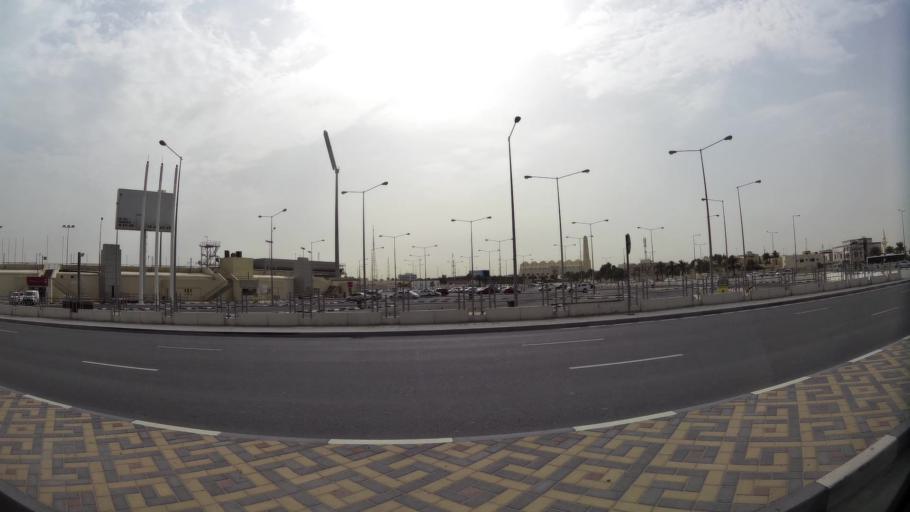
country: QA
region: Baladiyat ad Dawhah
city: Doha
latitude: 25.3190
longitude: 51.5129
